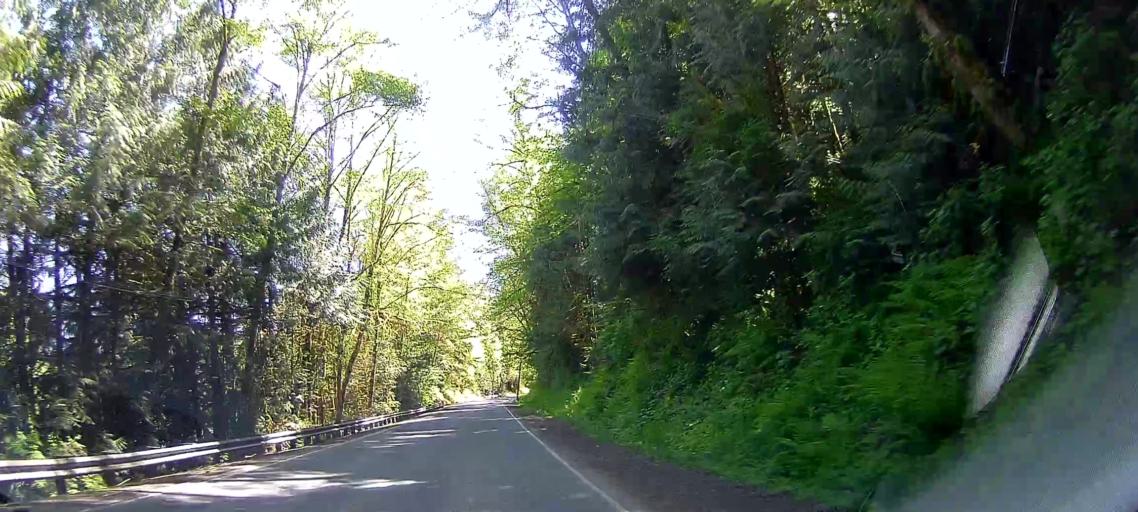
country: US
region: Washington
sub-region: Snohomish County
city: Darrington
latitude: 48.5190
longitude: -121.7647
